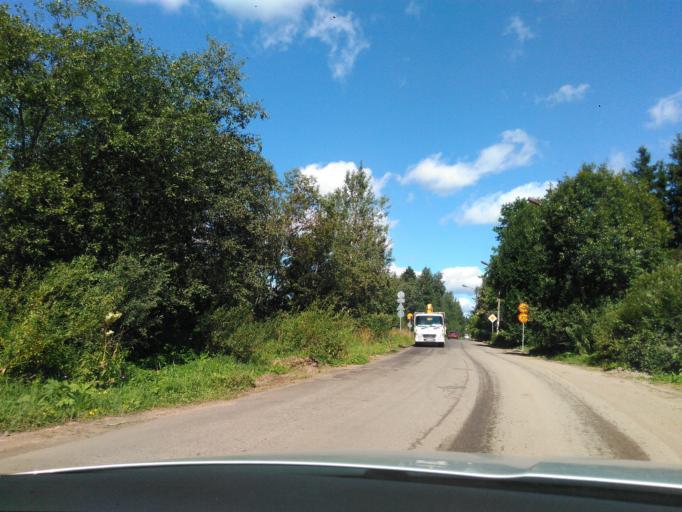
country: RU
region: Moskovskaya
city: Klin
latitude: 56.2361
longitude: 36.8364
